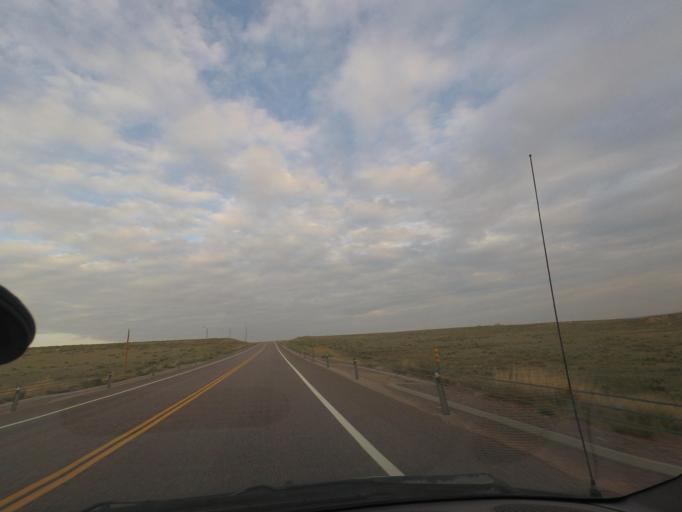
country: US
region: Kansas
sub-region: Cheyenne County
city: Saint Francis
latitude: 39.7468
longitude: -102.0815
